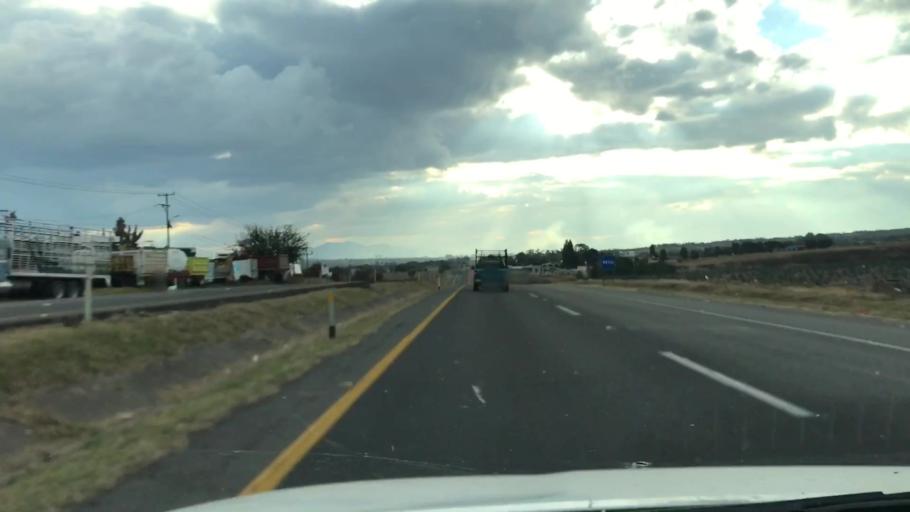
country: MX
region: Guanajuato
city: Penjamo
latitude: 20.4157
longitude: -101.7293
